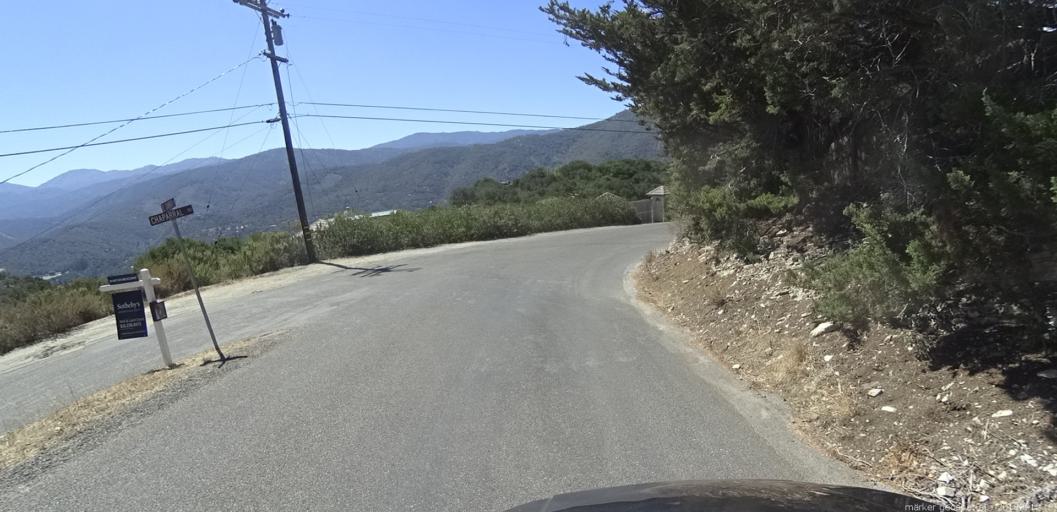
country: US
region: California
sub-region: Monterey County
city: Carmel Valley Village
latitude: 36.4889
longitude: -121.7246
